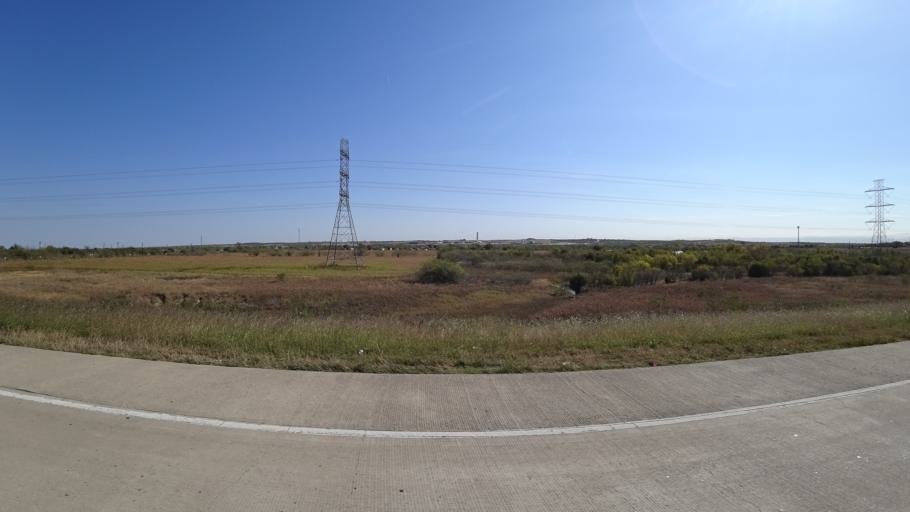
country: US
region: Texas
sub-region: Travis County
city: Garfield
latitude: 30.1469
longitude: -97.6602
